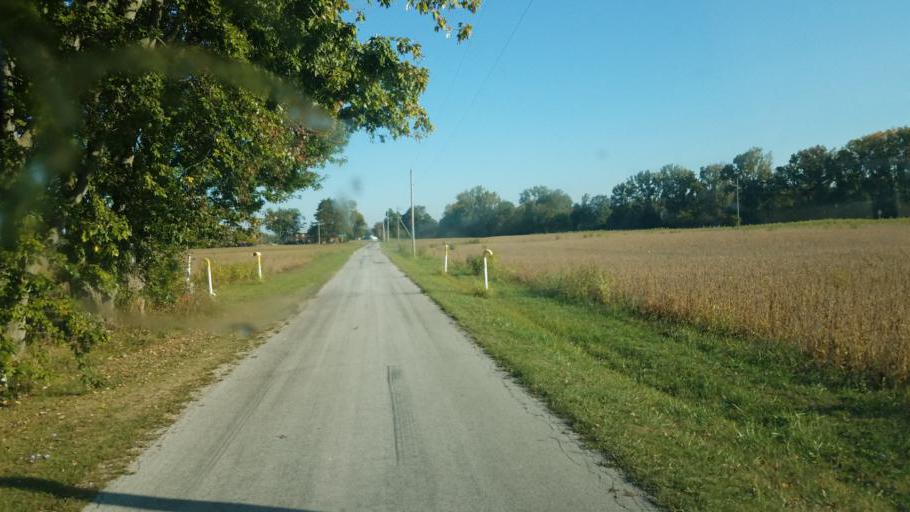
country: US
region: Ohio
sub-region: Union County
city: Richwood
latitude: 40.5499
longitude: -83.2684
